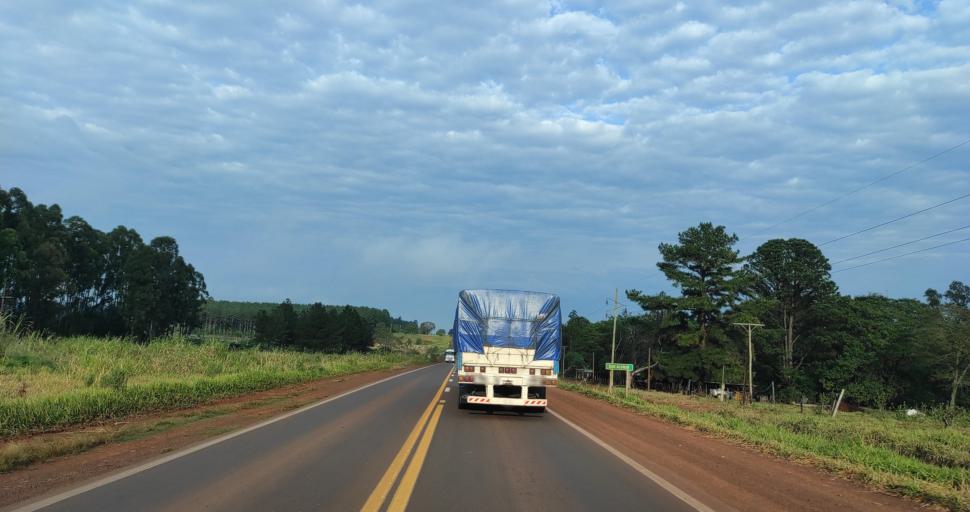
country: AR
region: Corrientes
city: Gobernador Ingeniero Valentin Virasoro
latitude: -27.9409
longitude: -55.9824
